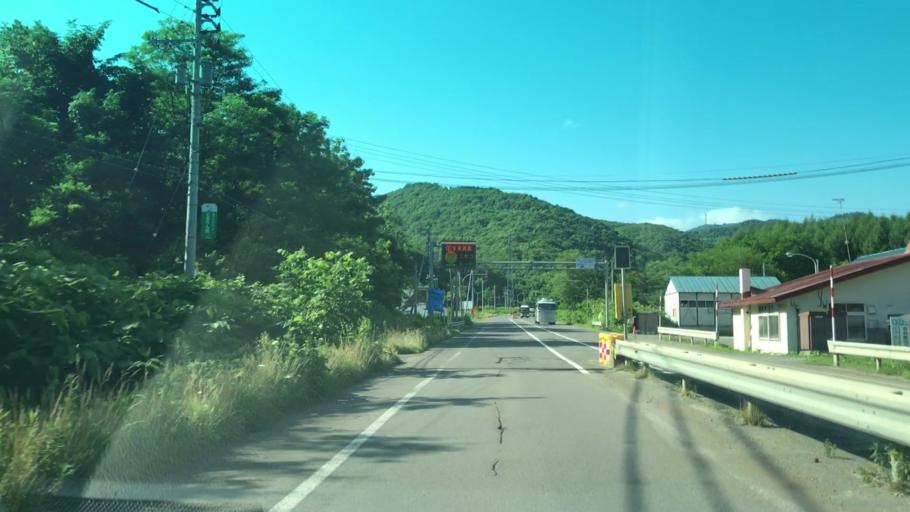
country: JP
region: Hokkaido
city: Iwanai
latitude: 43.0052
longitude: 140.6669
